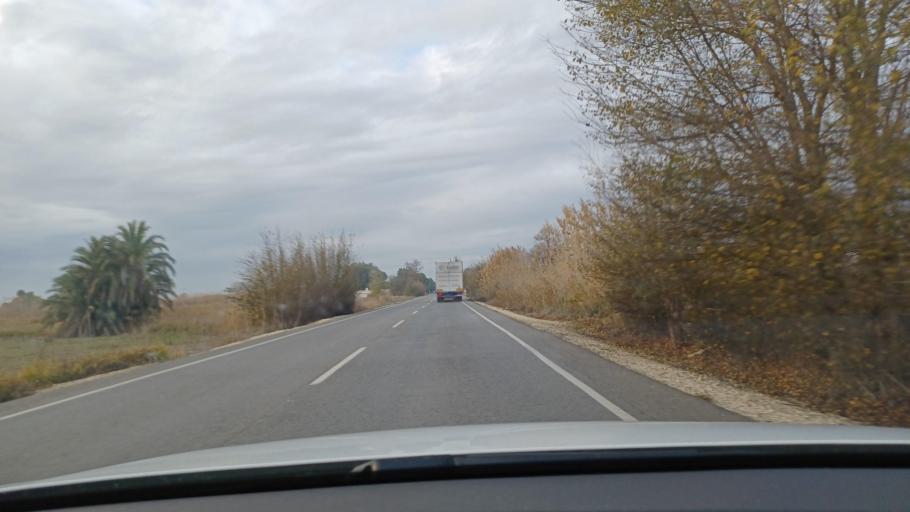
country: ES
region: Valencia
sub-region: Provincia de Alicante
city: Daya Vieja
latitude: 38.1561
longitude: -0.7076
